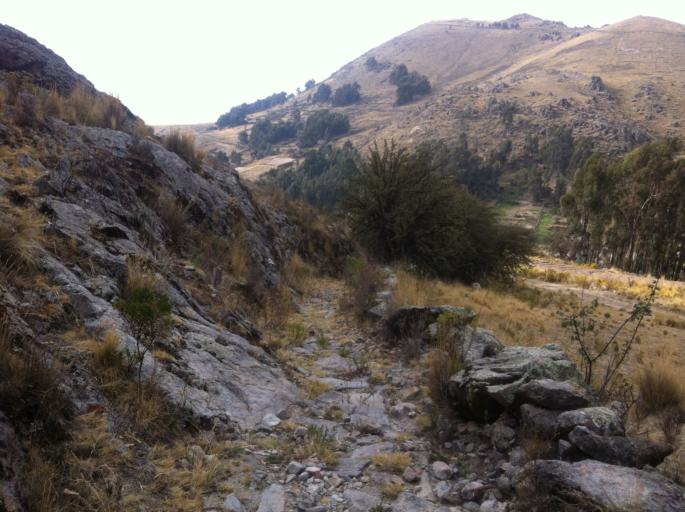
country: PE
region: Puno
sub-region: Yunguyo
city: Yunguyo
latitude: -16.1897
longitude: -69.0816
